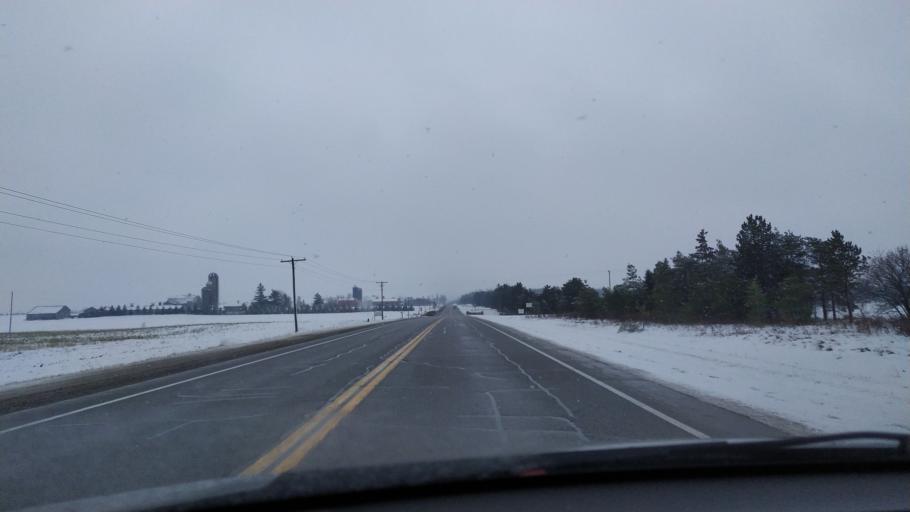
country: CA
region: Ontario
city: Waterloo
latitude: 43.6292
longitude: -80.7081
